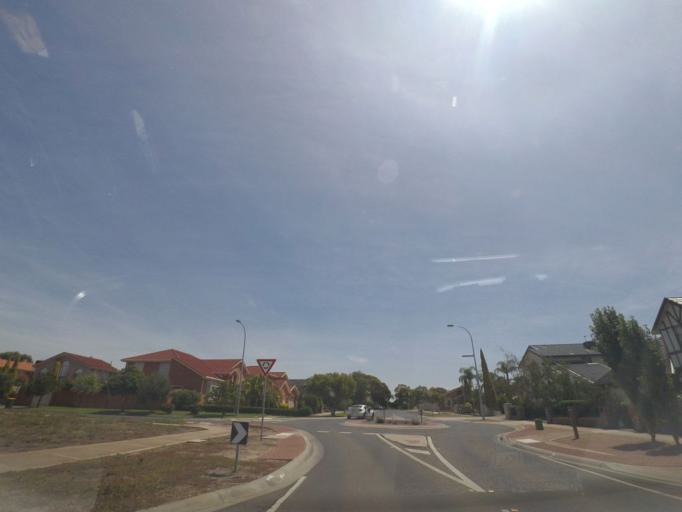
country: AU
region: Victoria
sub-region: Brimbank
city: Taylors Lakes
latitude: -37.7027
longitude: 144.7899
